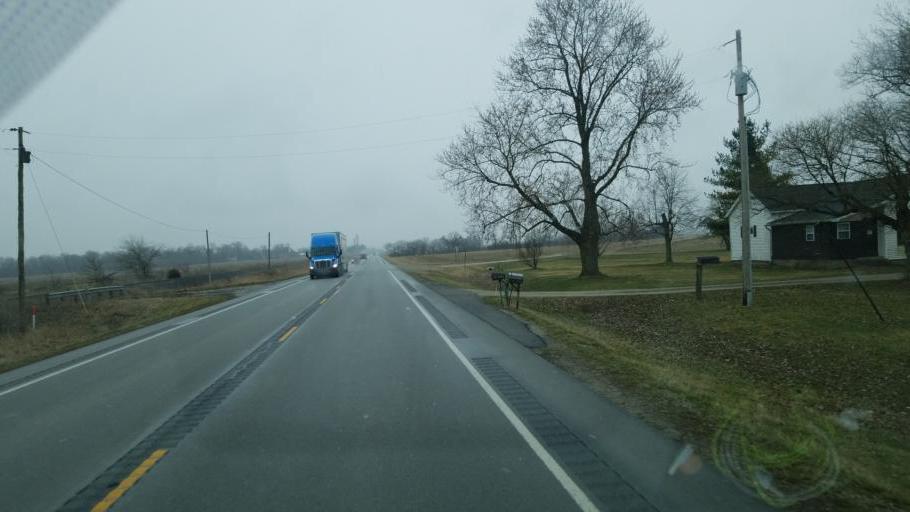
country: US
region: Indiana
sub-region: Wabash County
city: Wabash
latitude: 40.7346
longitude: -85.7904
